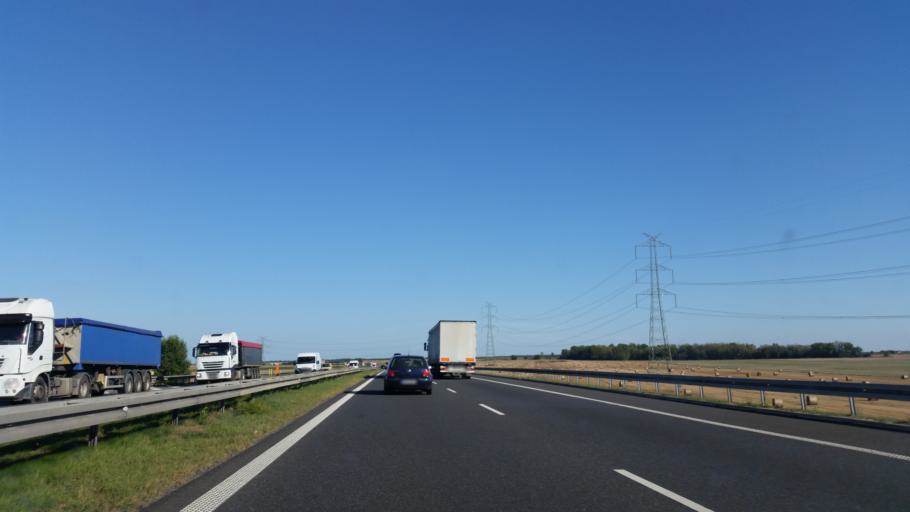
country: PL
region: Opole Voivodeship
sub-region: Powiat brzeski
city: Olszanka
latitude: 50.7483
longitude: 17.4460
